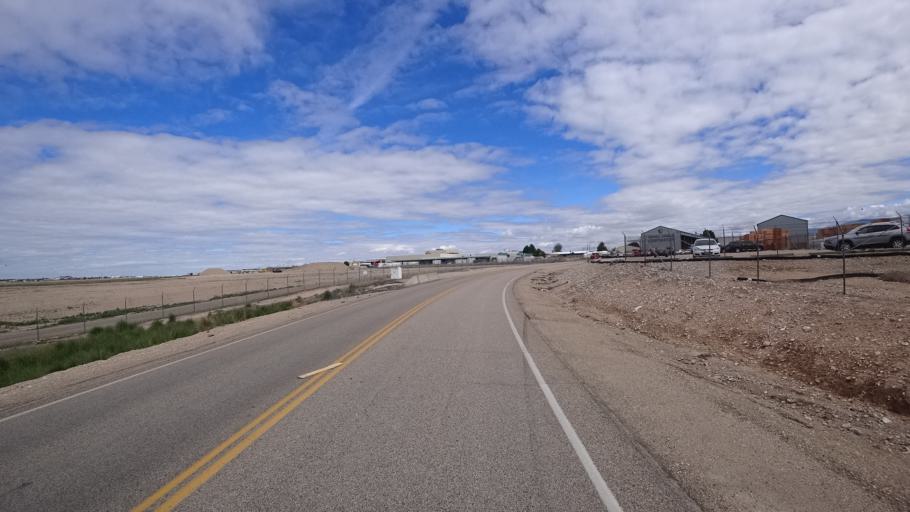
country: US
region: Idaho
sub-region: Ada County
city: Boise
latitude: 43.5570
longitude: -116.1935
